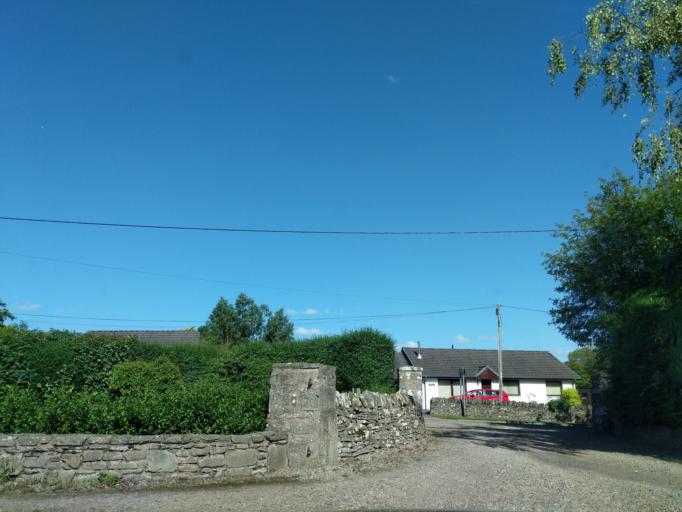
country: GB
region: Scotland
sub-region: Dundee City
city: Dundee
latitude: 56.5314
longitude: -2.9552
